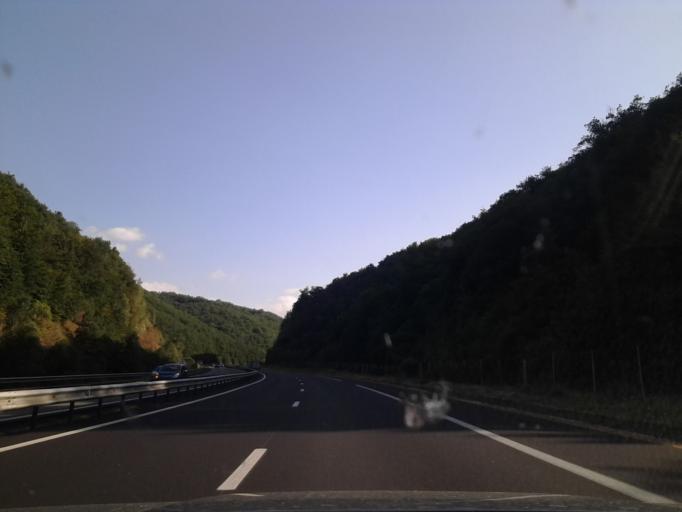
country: FR
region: Auvergne
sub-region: Departement du Cantal
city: Massiac
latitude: 45.1919
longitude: 3.1839
